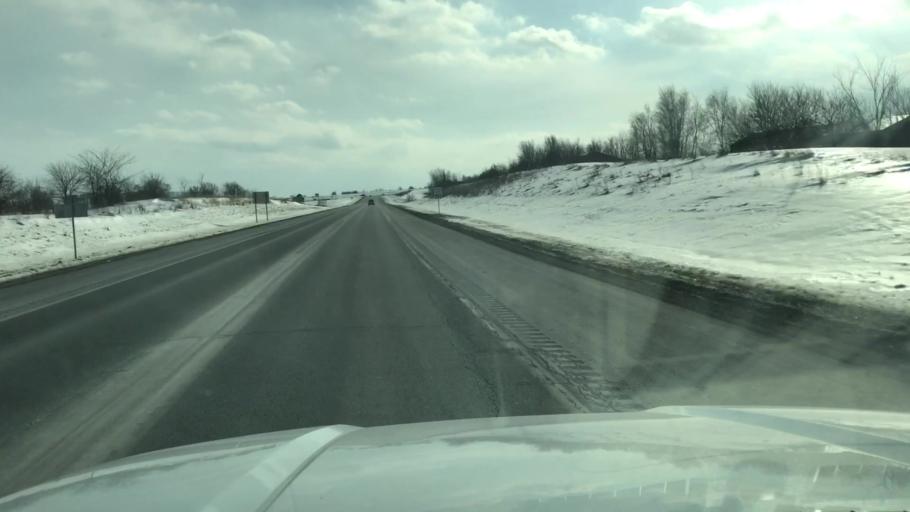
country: US
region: Missouri
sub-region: Nodaway County
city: Maryville
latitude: 40.3425
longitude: -94.8526
